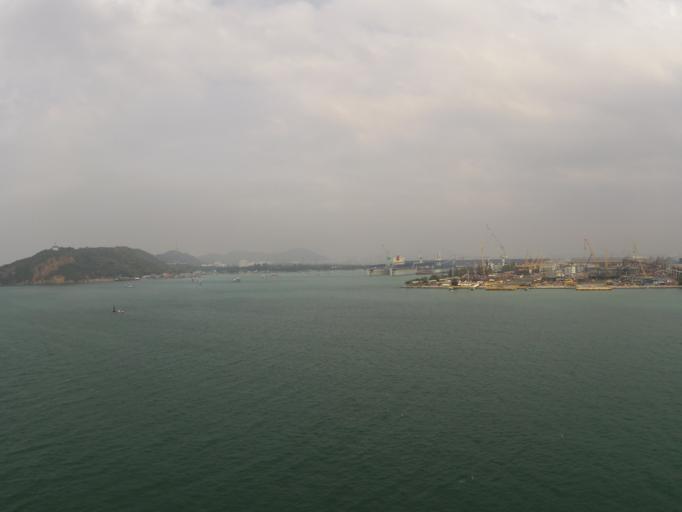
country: TH
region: Chon Buri
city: Bang Lamung
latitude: 13.0667
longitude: 100.8754
